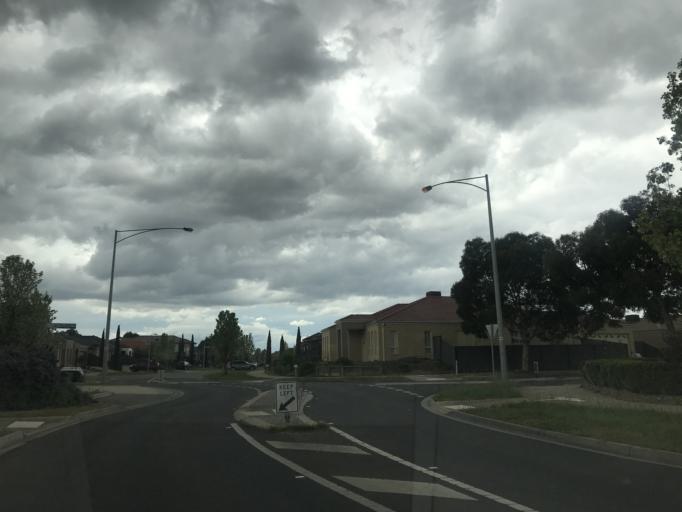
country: AU
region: Victoria
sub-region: Brimbank
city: Derrimut
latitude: -37.7900
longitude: 144.7562
